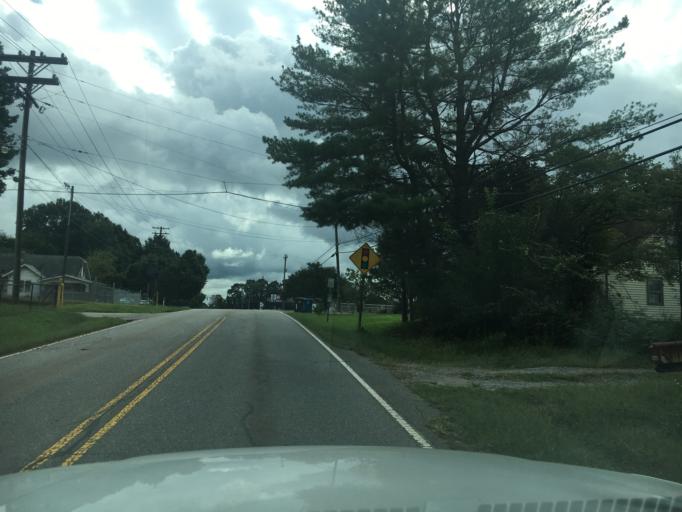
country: US
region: North Carolina
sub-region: Catawba County
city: Saint Stephens
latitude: 35.7239
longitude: -81.2660
